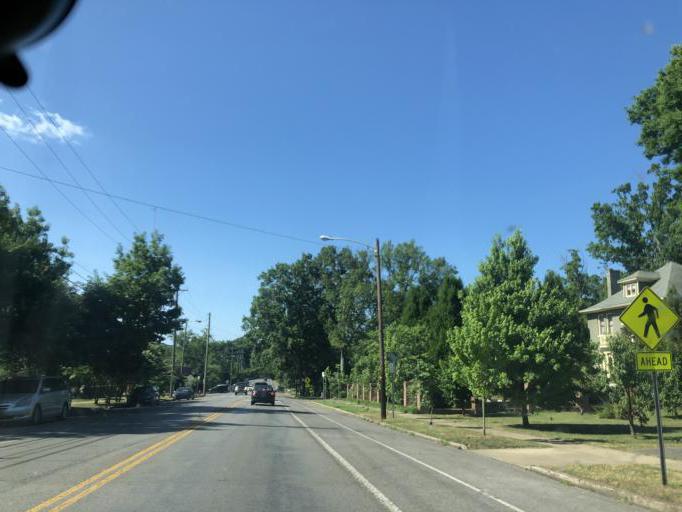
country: US
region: Tennessee
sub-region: Davidson County
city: Oak Hill
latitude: 36.1244
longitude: -86.7944
